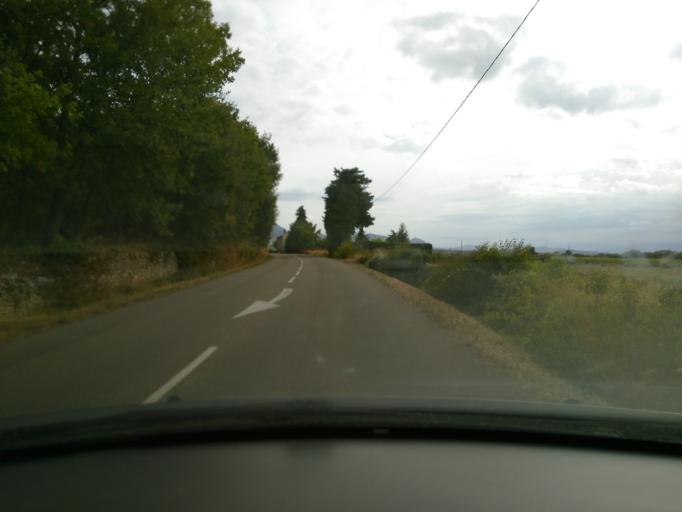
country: FR
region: Rhone-Alpes
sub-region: Departement de la Drome
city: Taulignan
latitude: 44.4445
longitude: 4.9885
